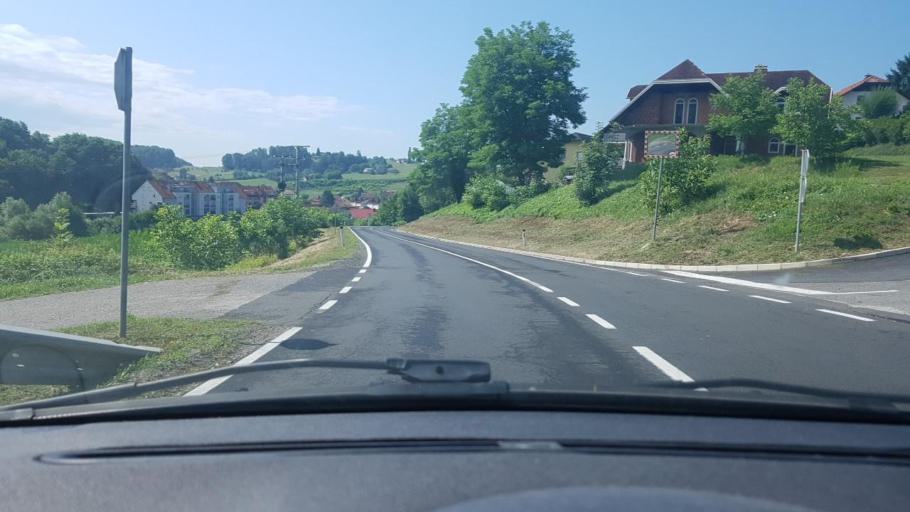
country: SI
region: Sentilj
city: Sentilj v Slov. Goricah
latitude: 46.6830
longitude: 15.6546
